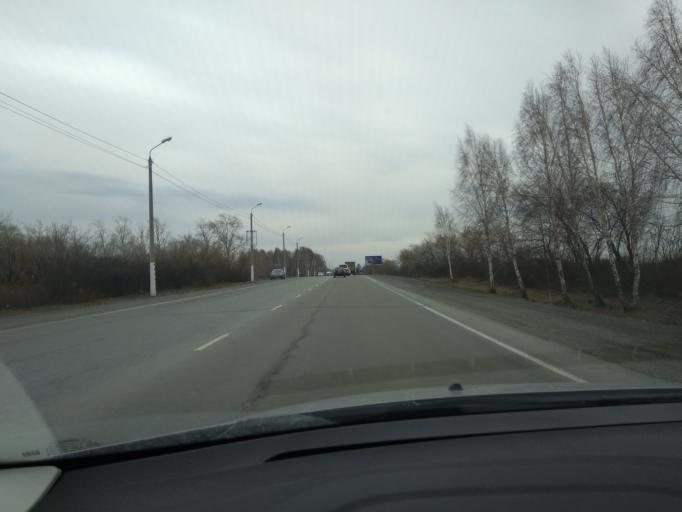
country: RU
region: Chelyabinsk
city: Potanino
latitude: 55.2923
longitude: 61.5111
